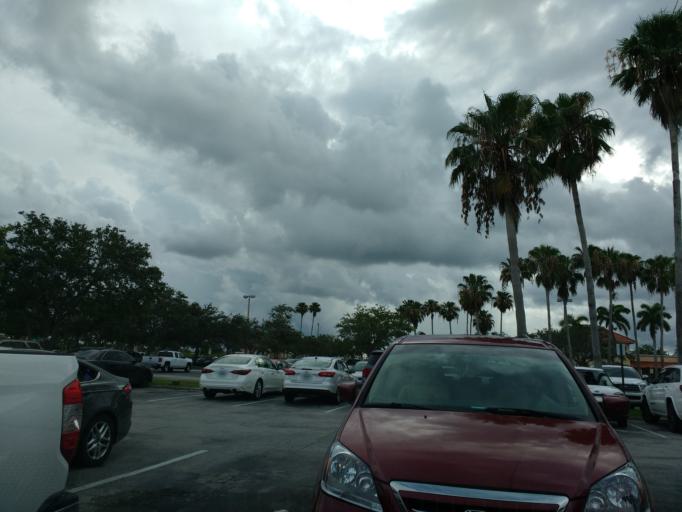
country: US
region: Florida
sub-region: Miami-Dade County
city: Florida City
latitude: 25.4516
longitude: -80.4727
